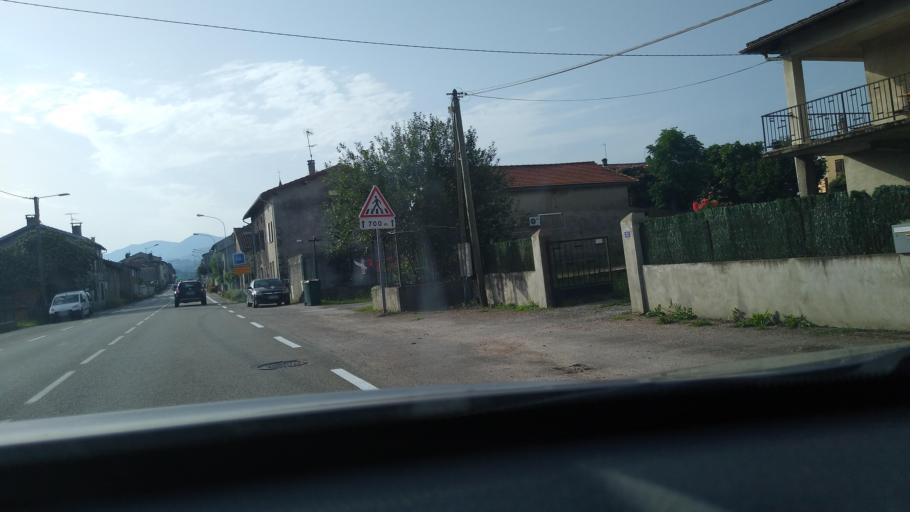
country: FR
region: Midi-Pyrenees
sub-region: Departement de l'Ariege
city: Saint-Lizier
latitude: 43.0105
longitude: 1.1171
